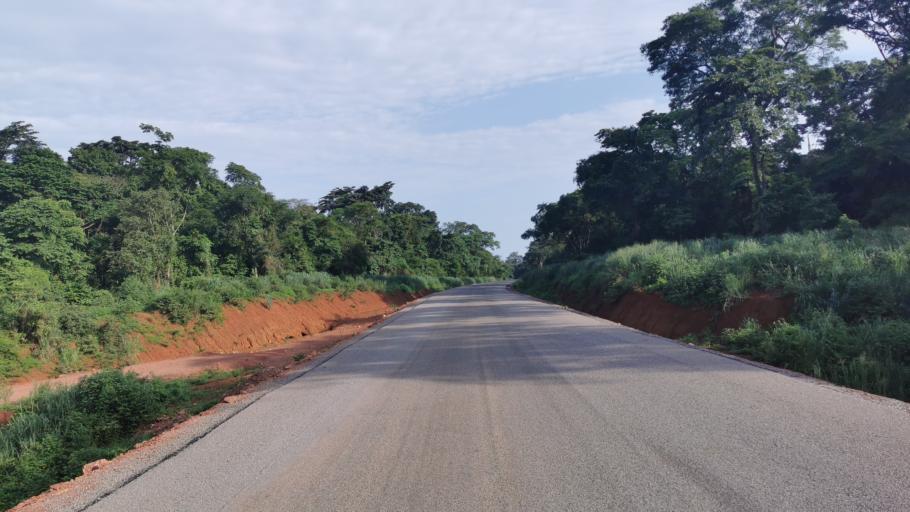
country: ET
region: Gambela
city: Gambela
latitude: 7.7187
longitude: 34.6614
